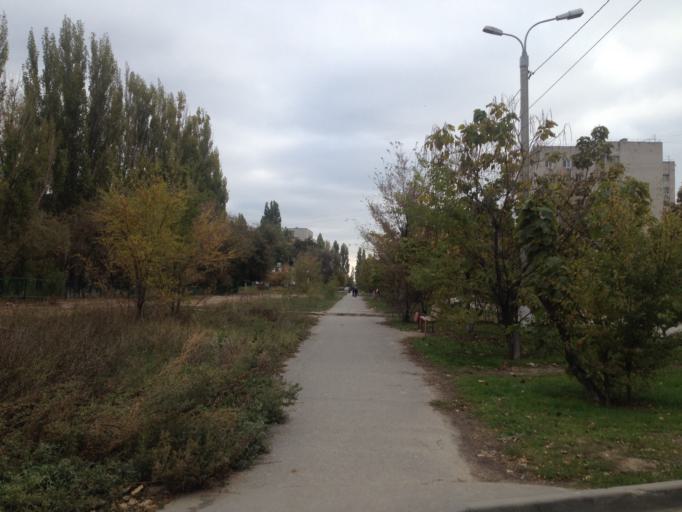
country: RU
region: Volgograd
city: Volgograd
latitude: 48.7382
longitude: 44.4872
